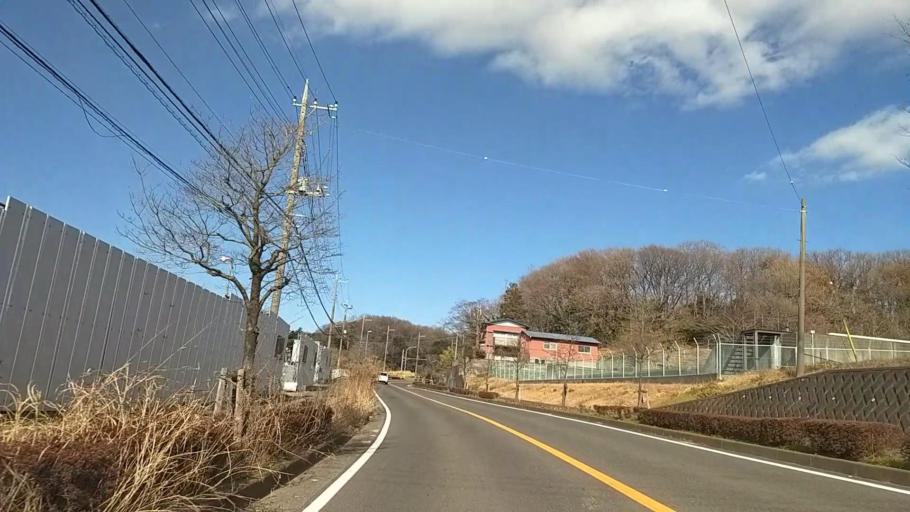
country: JP
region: Kanagawa
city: Isehara
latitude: 35.4247
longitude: 139.3026
